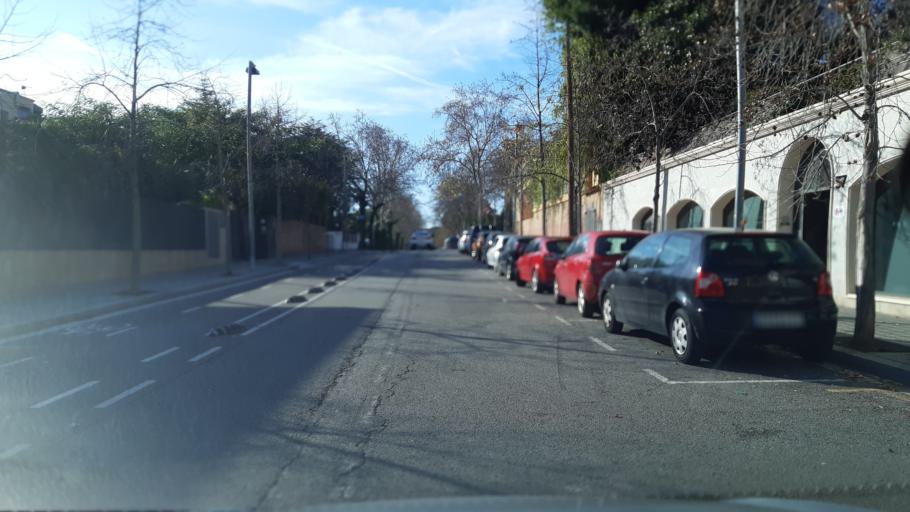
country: ES
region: Catalonia
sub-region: Provincia de Barcelona
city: les Corts
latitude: 41.3903
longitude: 2.1112
